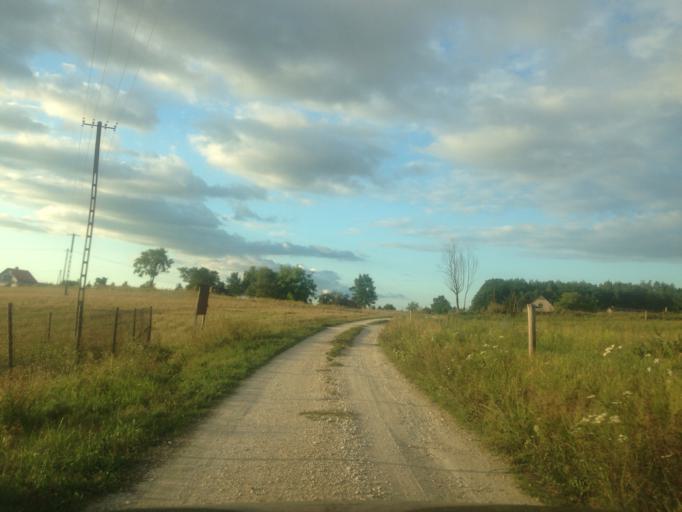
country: PL
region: Kujawsko-Pomorskie
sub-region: Powiat brodnicki
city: Gorzno
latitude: 53.2009
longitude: 19.6621
